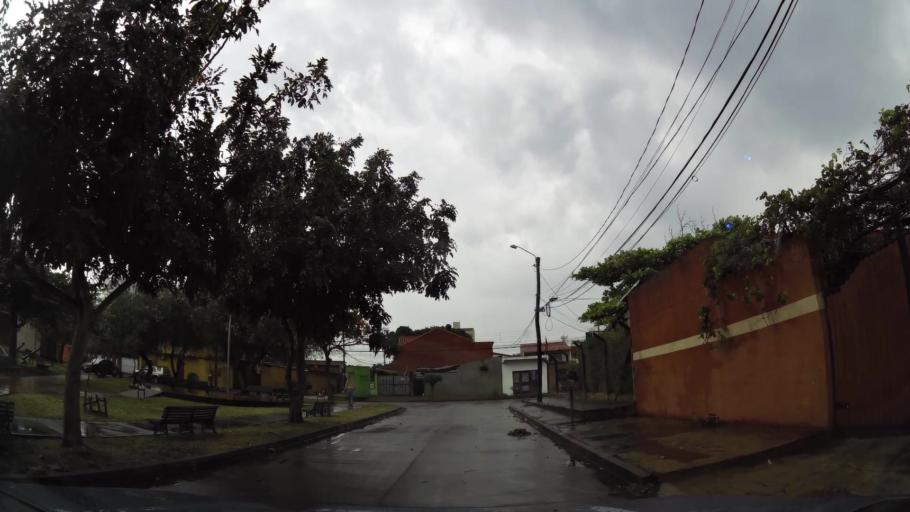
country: BO
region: Santa Cruz
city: Santa Cruz de la Sierra
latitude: -17.7957
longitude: -63.1534
